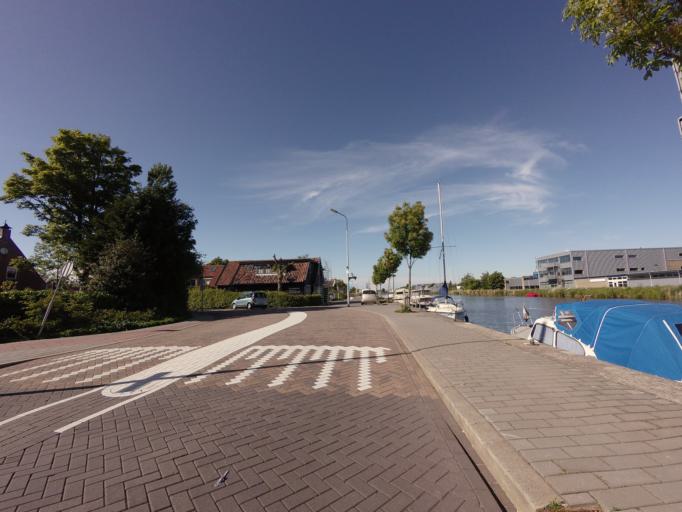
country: NL
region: North Holland
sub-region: Gemeente Zaanstad
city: Zaanstad
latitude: 52.5024
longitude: 4.7753
